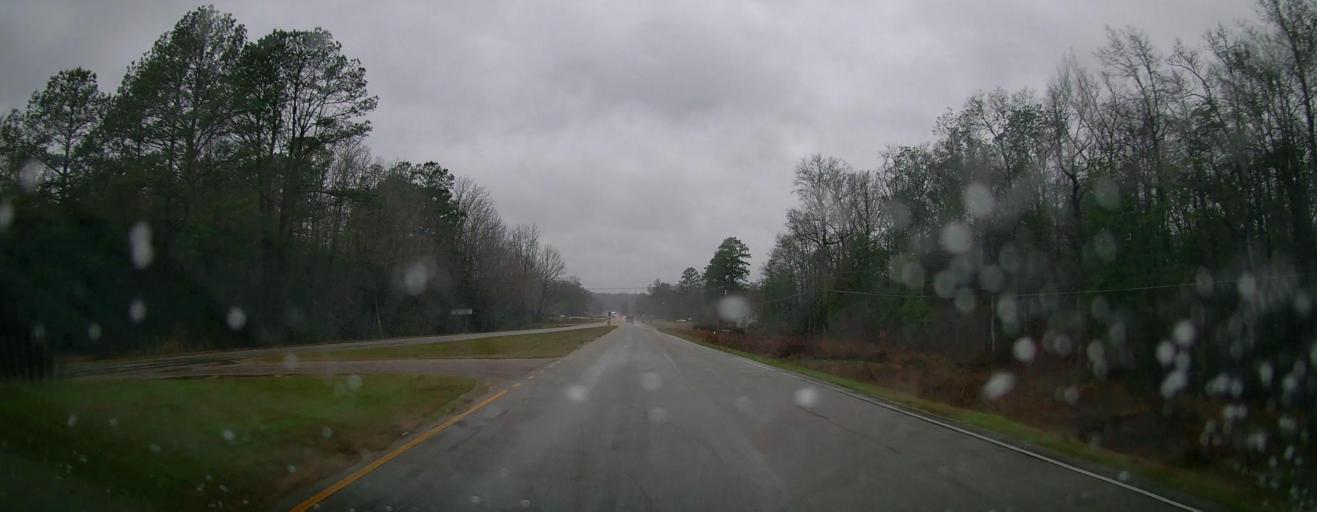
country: US
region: Alabama
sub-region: Autauga County
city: Prattville
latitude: 32.4683
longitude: -86.5024
